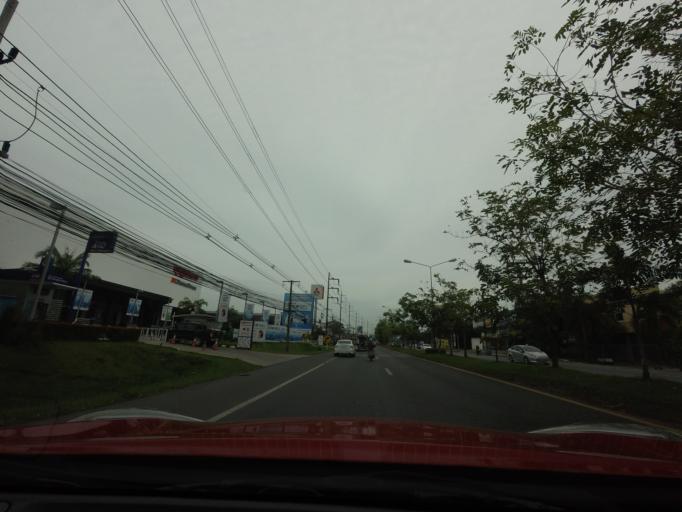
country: TH
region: Songkhla
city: Hat Yai
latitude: 6.9823
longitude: 100.4795
